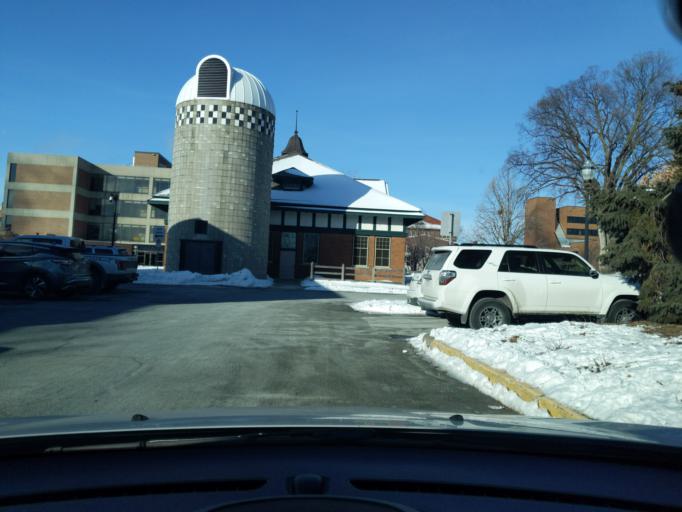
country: US
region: Minnesota
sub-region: Ramsey County
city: Falcon Heights
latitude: 44.9826
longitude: -93.1824
